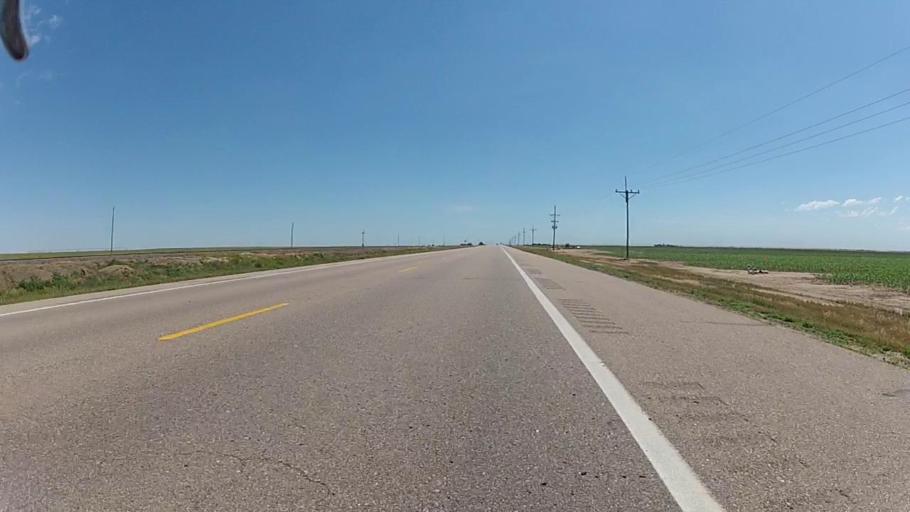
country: US
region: Kansas
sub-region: Gray County
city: Cimarron
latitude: 37.6617
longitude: -100.2131
